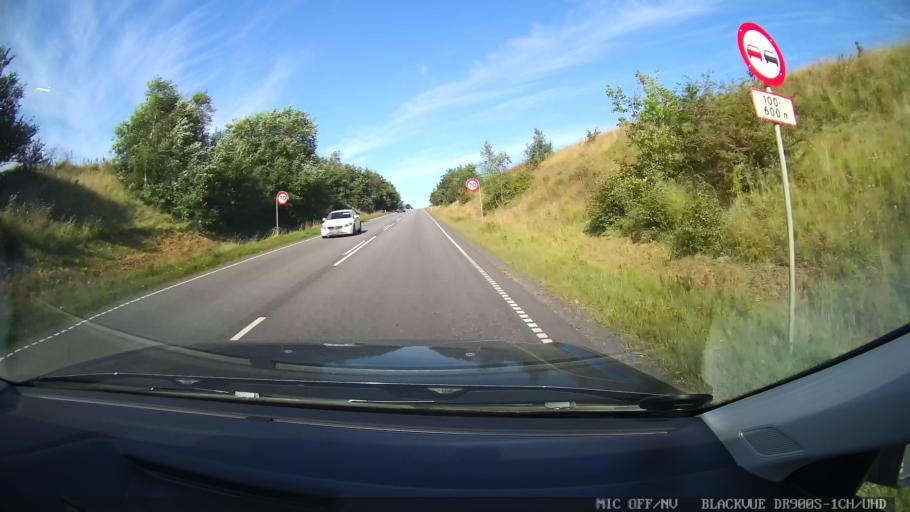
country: DK
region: North Denmark
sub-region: Mariagerfjord Kommune
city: Hobro
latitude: 56.6594
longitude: 9.7856
